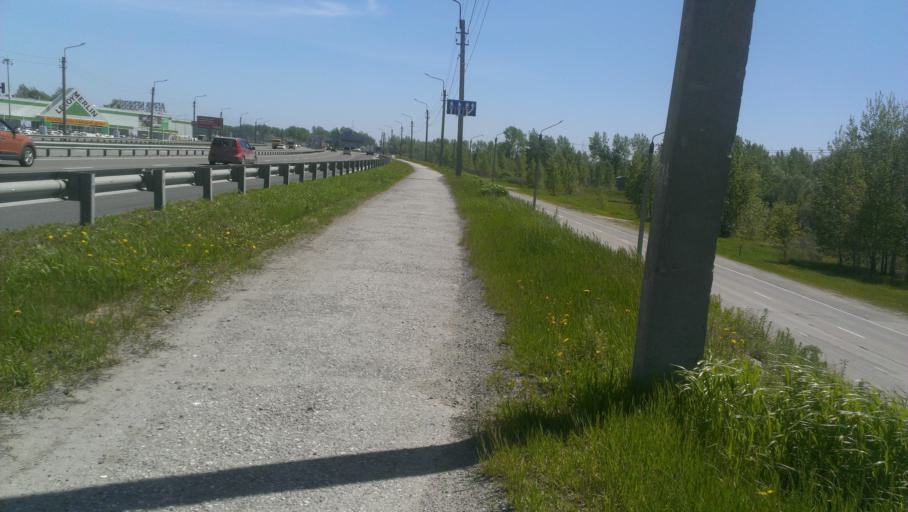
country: RU
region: Altai Krai
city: Zaton
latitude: 53.3162
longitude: 83.8246
